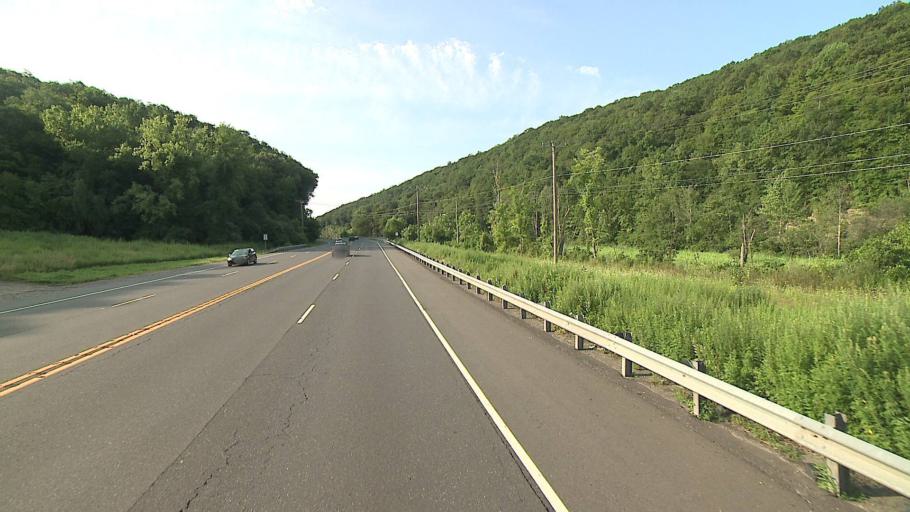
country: US
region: Connecticut
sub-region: Fairfield County
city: Danbury
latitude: 41.3635
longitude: -73.4735
